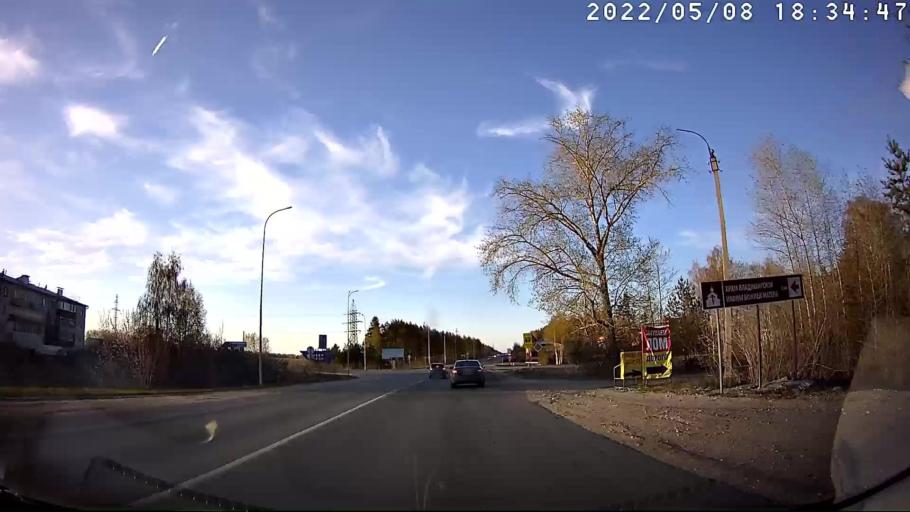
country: RU
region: Mariy-El
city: Volzhsk
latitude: 55.9025
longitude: 48.3566
